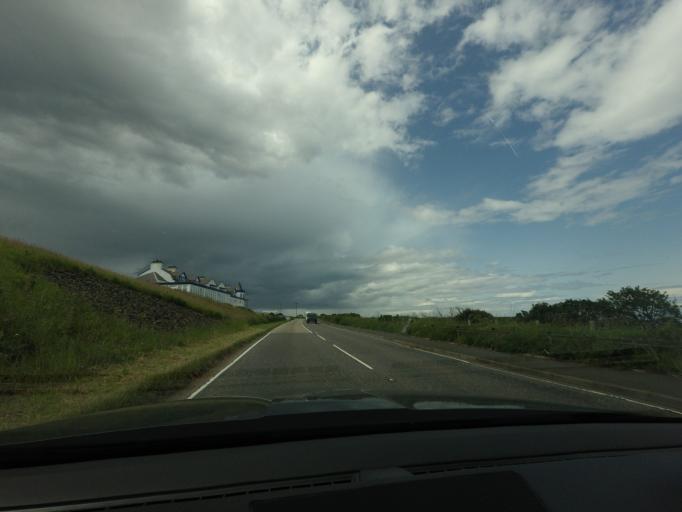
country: GB
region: Scotland
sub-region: Moray
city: Cullen
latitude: 57.6924
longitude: -2.8386
